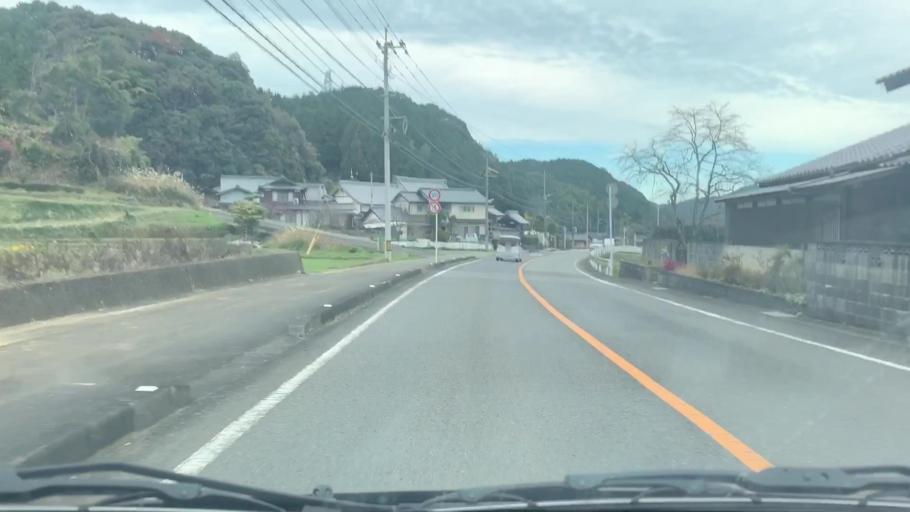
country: JP
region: Saga Prefecture
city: Takeocho-takeo
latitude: 33.1763
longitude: 129.9709
